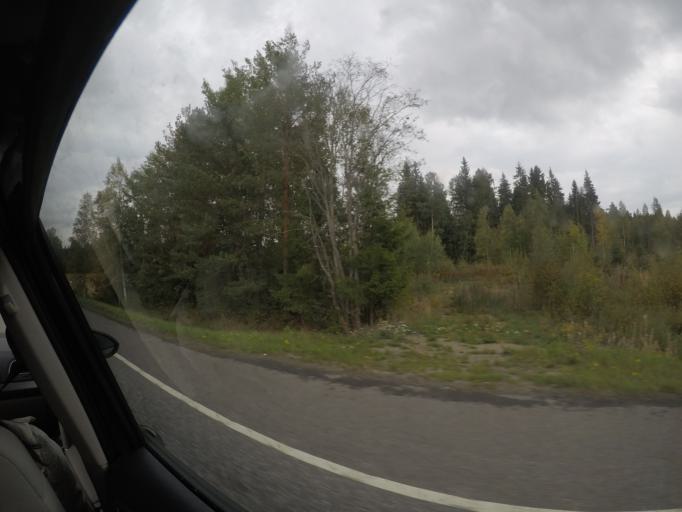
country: FI
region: Haeme
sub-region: Haemeenlinna
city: Parola
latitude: 61.1784
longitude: 24.4126
